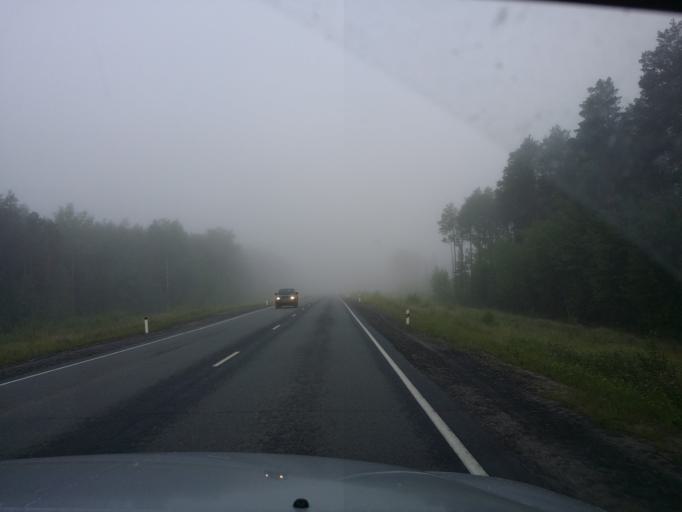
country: RU
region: Khanty-Mansiyskiy Avtonomnyy Okrug
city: Gornopravdinsk
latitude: 59.6448
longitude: 69.8863
